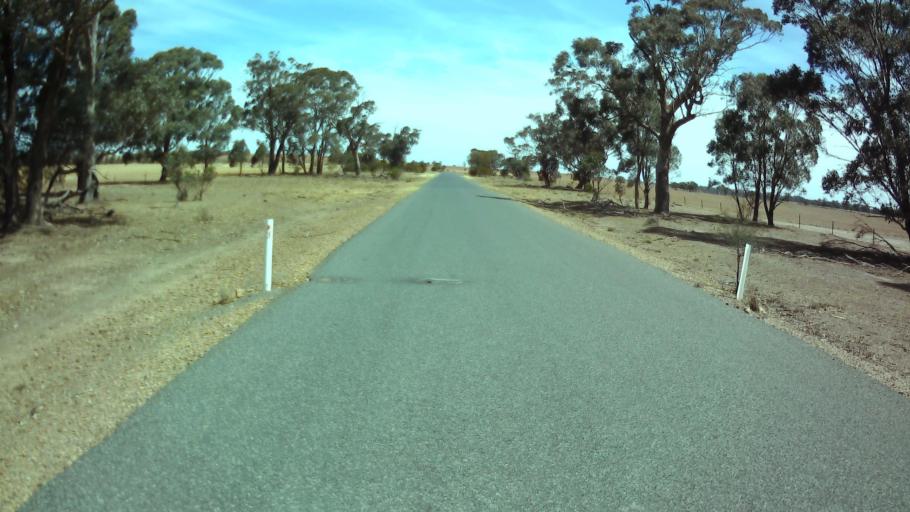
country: AU
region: New South Wales
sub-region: Weddin
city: Grenfell
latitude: -33.8838
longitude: 147.7424
